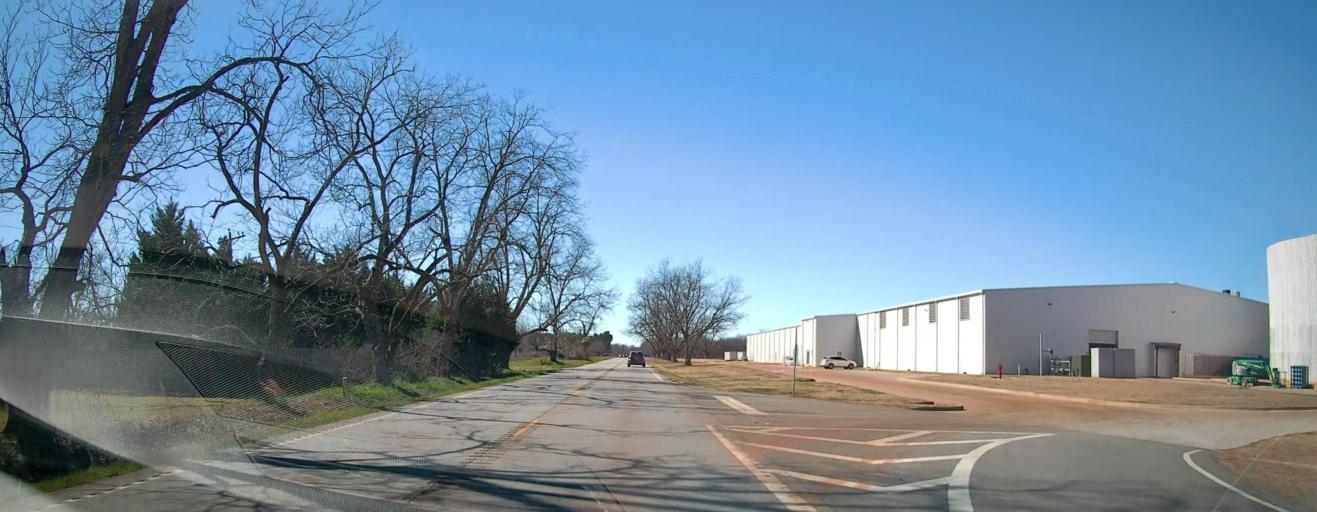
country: US
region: Georgia
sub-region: Peach County
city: Fort Valley
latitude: 32.5540
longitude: -83.8126
